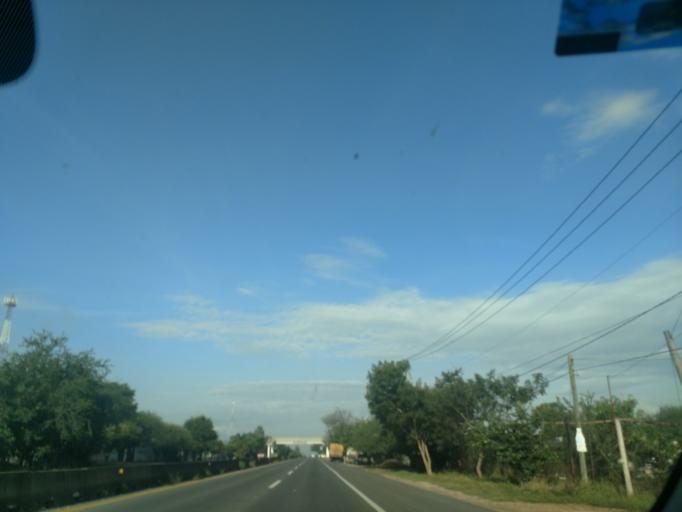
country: MX
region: Jalisco
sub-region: Ameca
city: Los Pocitos
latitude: 20.5372
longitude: -103.9354
